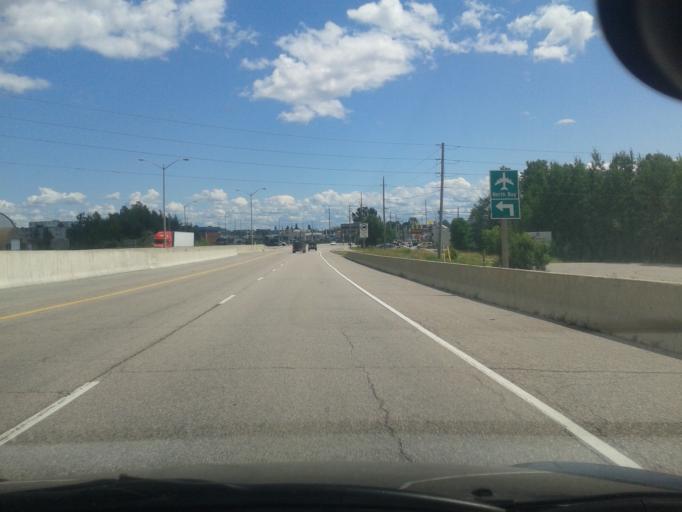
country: CA
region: Ontario
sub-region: Nipissing District
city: North Bay
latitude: 46.3367
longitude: -79.4673
